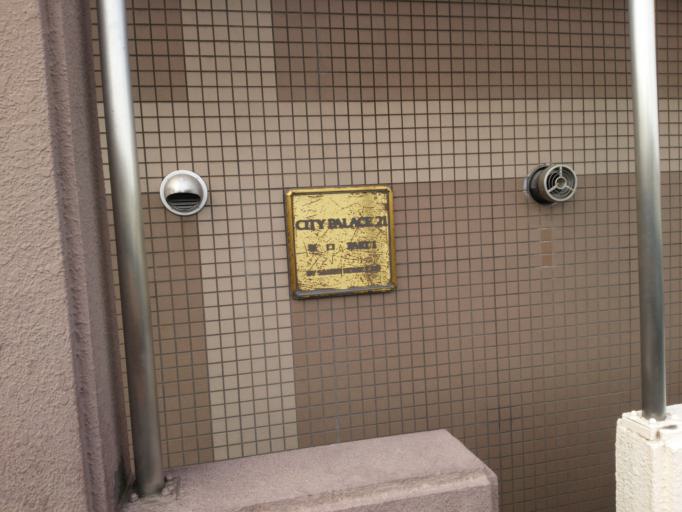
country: JP
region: Hyogo
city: Amagasaki
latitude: 34.7466
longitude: 135.4110
